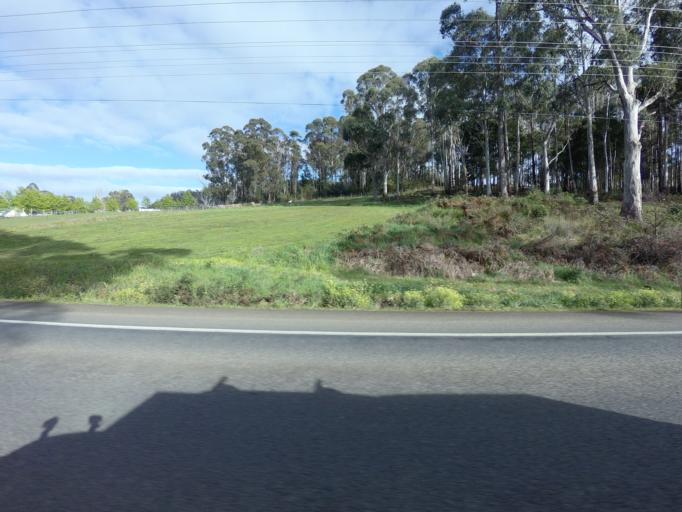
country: AU
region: Tasmania
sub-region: Huon Valley
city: Huonville
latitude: -43.0592
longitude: 147.0292
